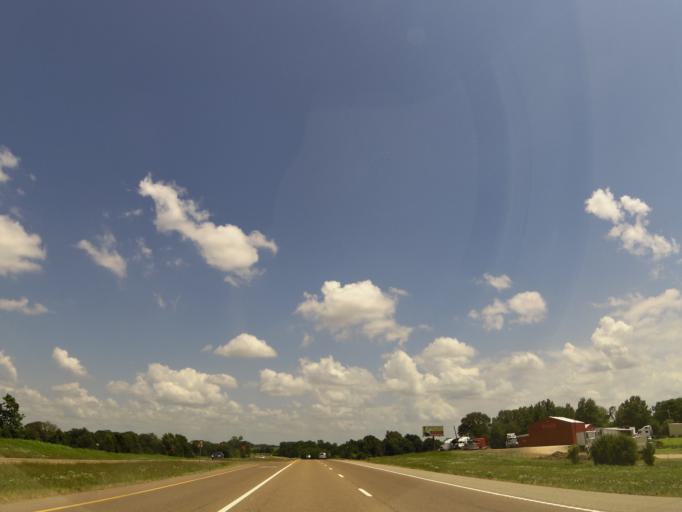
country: US
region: Tennessee
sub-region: Crockett County
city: Alamo
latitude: 35.7815
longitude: -89.1418
